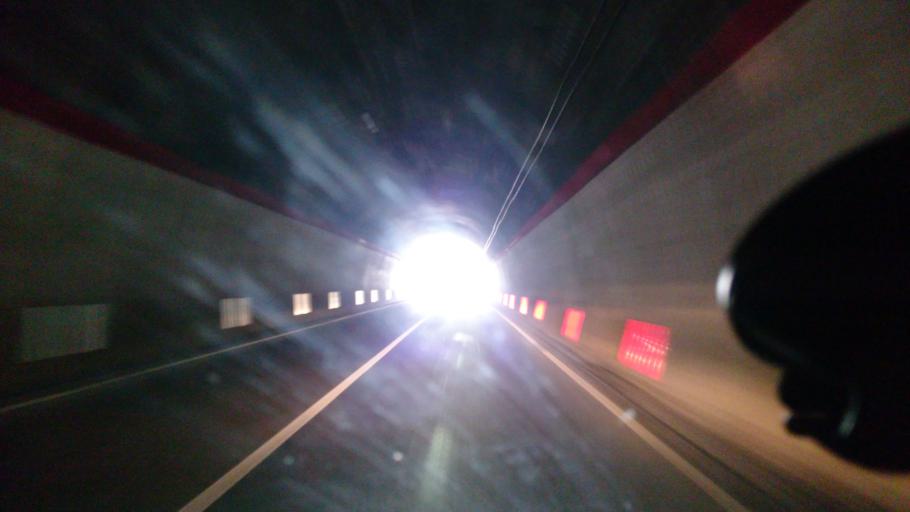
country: IT
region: Calabria
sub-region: Provincia di Cosenza
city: Cittadella del Capo
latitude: 39.5567
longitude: 15.8783
